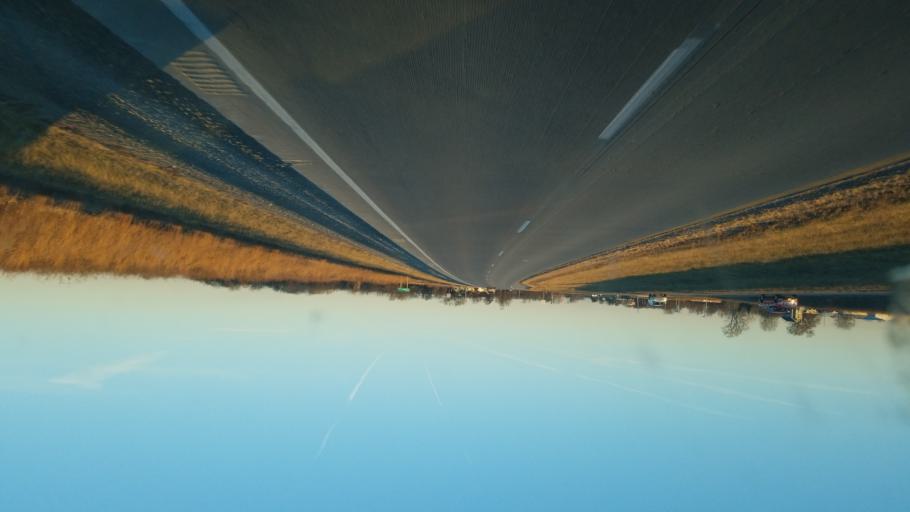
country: US
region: Iowa
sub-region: Jefferson County
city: Fairfield
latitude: 41.0140
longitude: -92.0654
